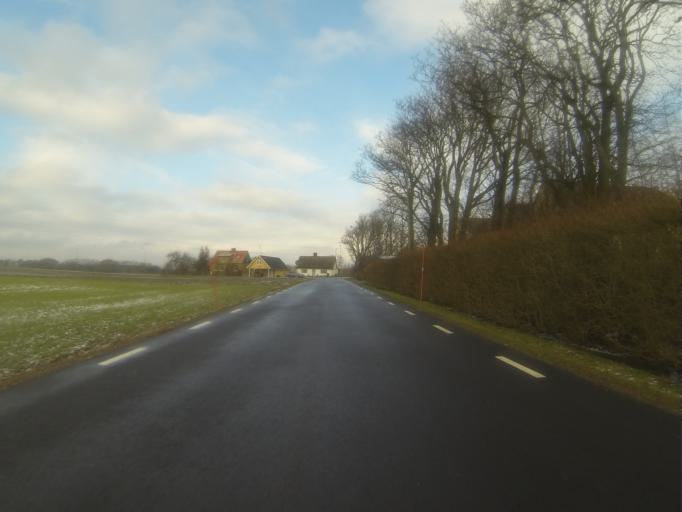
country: SE
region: Skane
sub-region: Svedala Kommun
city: Klagerup
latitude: 55.6235
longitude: 13.3105
